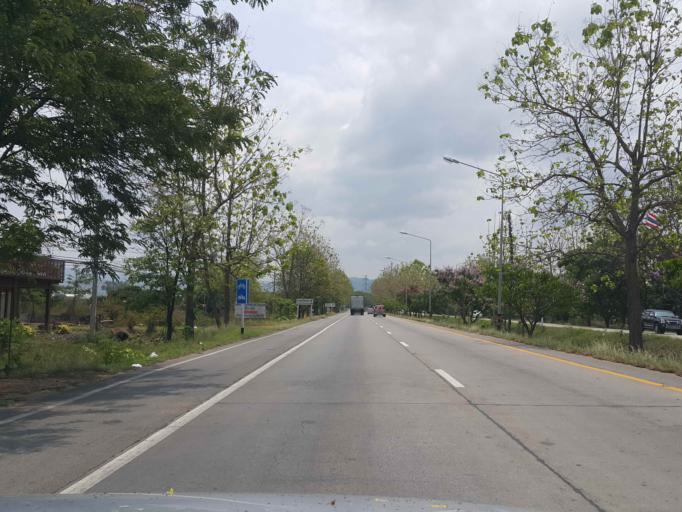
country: TH
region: Lamphun
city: Lamphun
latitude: 18.5405
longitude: 99.0678
